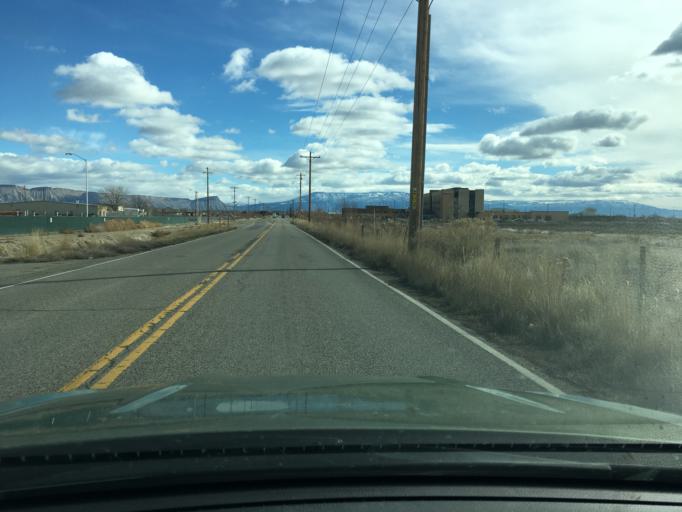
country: US
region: Colorado
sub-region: Mesa County
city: Redlands
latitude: 39.1062
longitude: -108.6201
